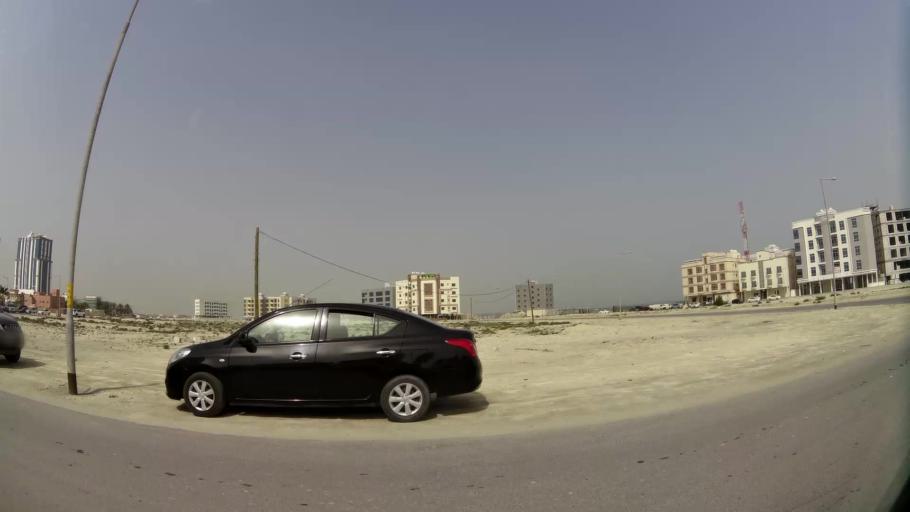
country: BH
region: Manama
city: Jidd Hafs
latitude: 26.2391
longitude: 50.5300
